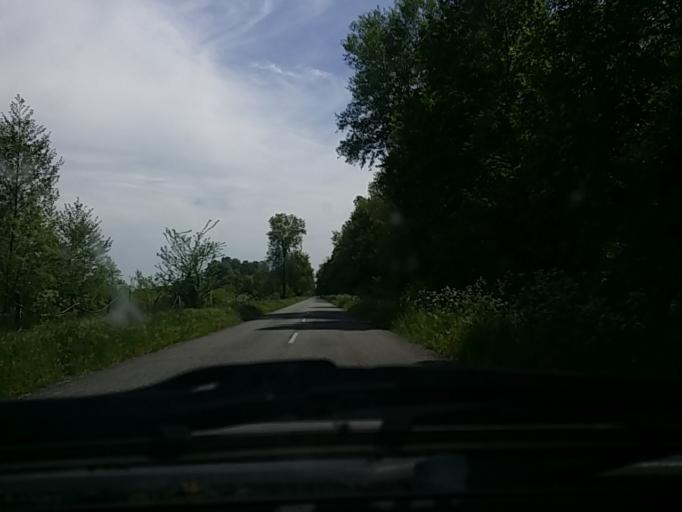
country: HU
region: Baranya
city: Sellye
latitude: 45.9161
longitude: 17.6696
